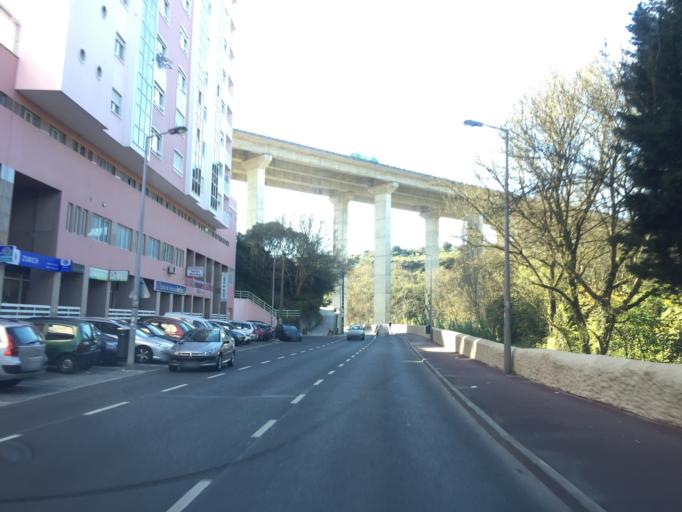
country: PT
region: Lisbon
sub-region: Sintra
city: Belas
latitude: 38.7739
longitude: -9.2609
